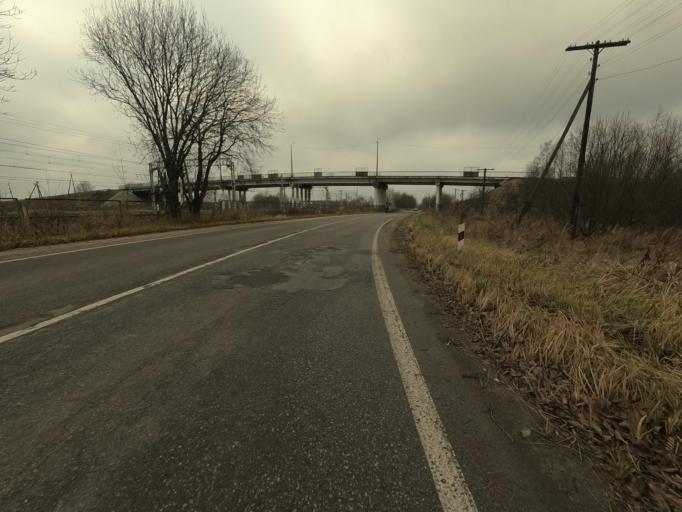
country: RU
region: Leningrad
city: Lyuban'
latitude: 59.4877
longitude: 31.2669
